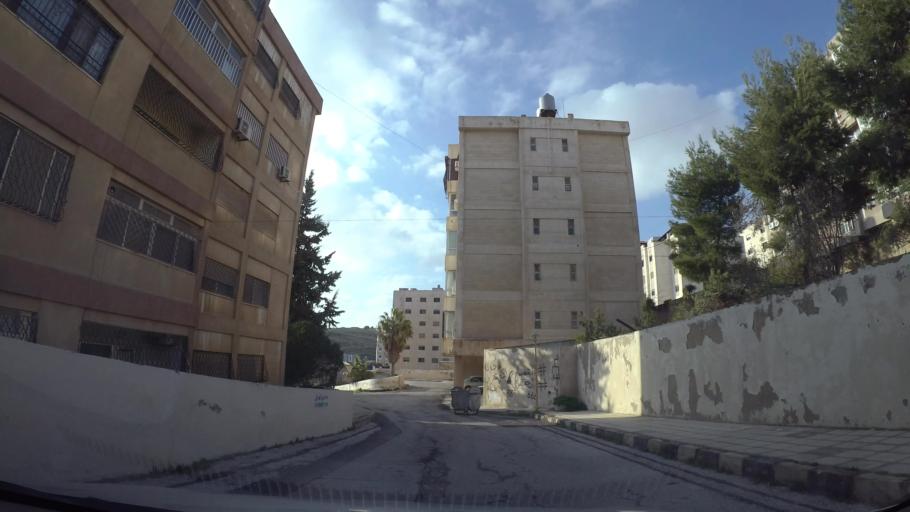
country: JO
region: Amman
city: Al Jubayhah
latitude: 32.0089
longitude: 35.8625
